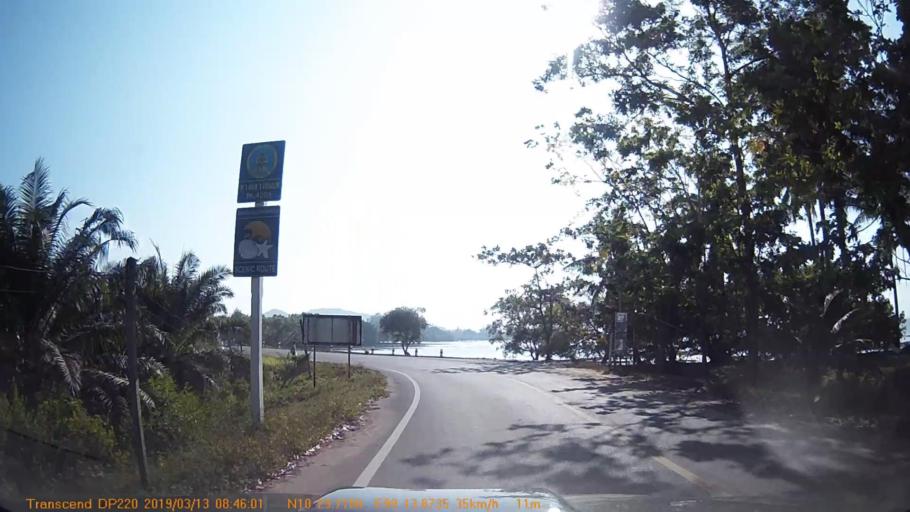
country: TH
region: Chumphon
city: Chumphon
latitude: 10.4953
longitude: 99.2315
